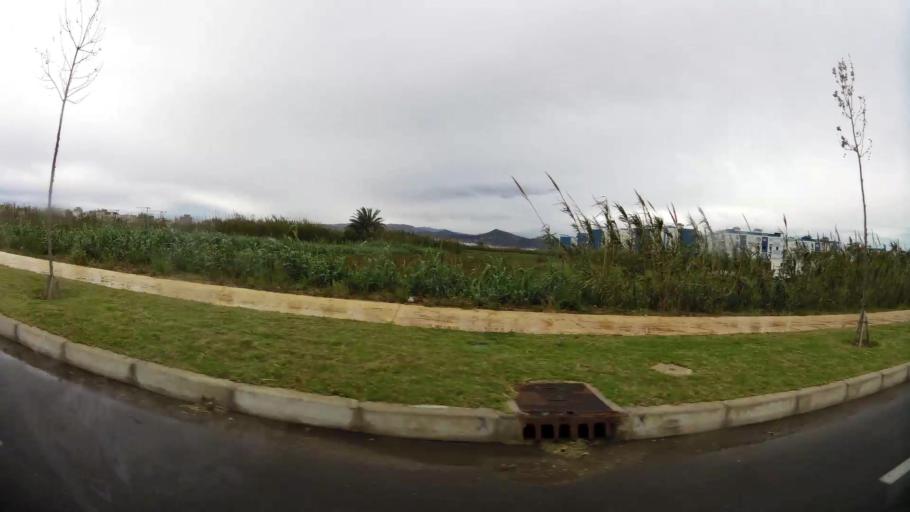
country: MA
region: Tanger-Tetouan
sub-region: Tetouan
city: Martil
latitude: 35.6282
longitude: -5.2980
